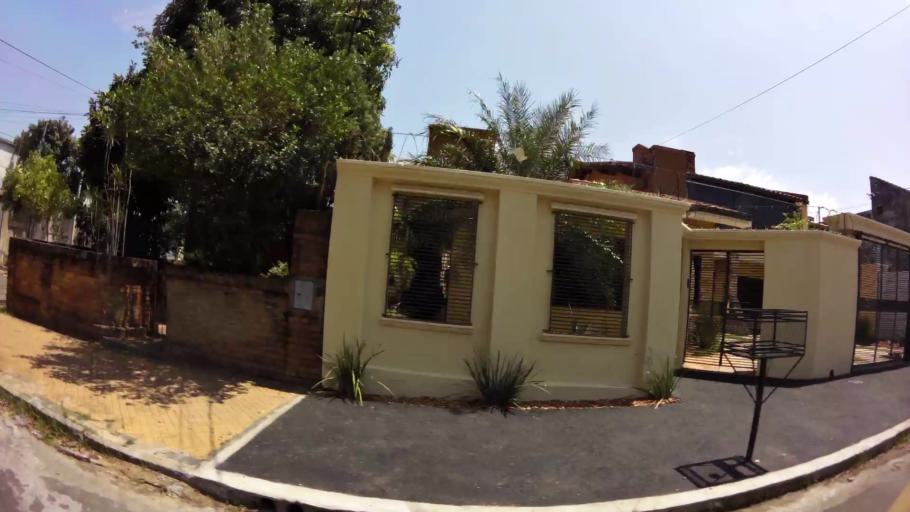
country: PY
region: Asuncion
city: Asuncion
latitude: -25.2972
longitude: -57.6426
